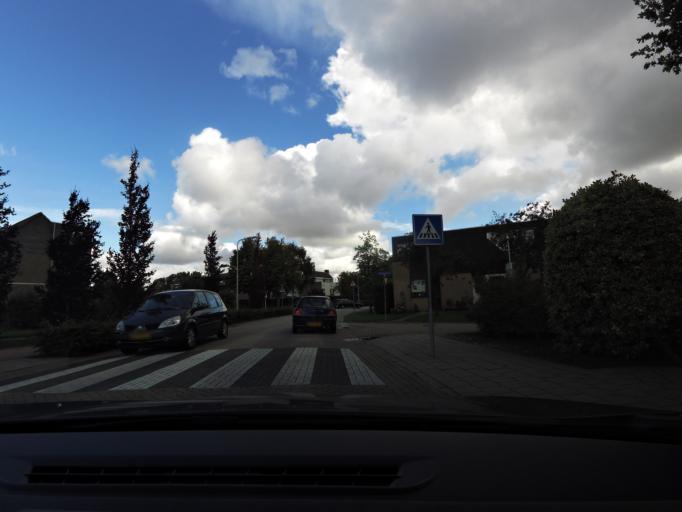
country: NL
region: South Holland
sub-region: Gemeente Oud-Beijerland
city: Oud-Beijerland
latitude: 51.8252
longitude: 4.4230
